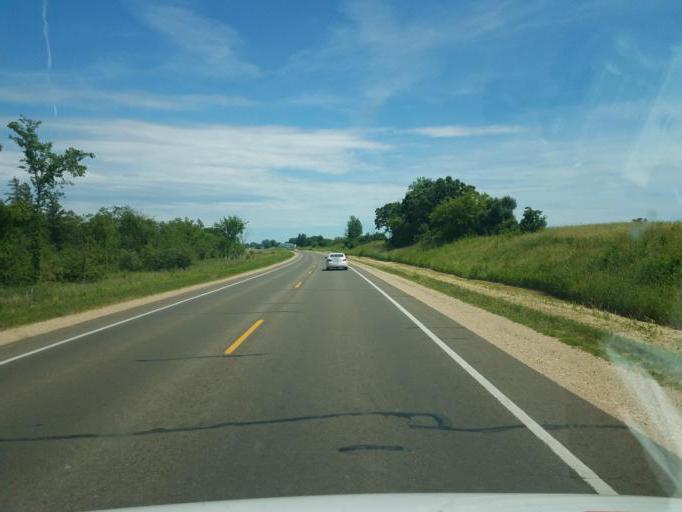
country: US
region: Wisconsin
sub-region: Sauk County
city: Reedsburg
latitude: 43.5444
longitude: -90.0483
